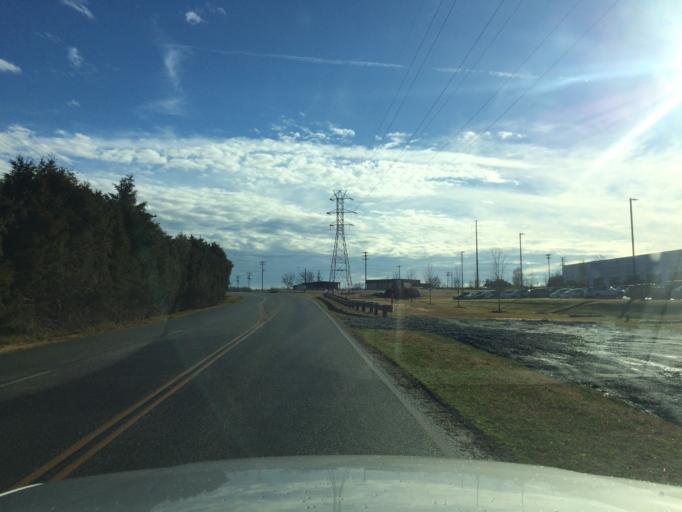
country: US
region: South Carolina
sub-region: Spartanburg County
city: Fairforest
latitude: 34.9632
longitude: -82.0371
